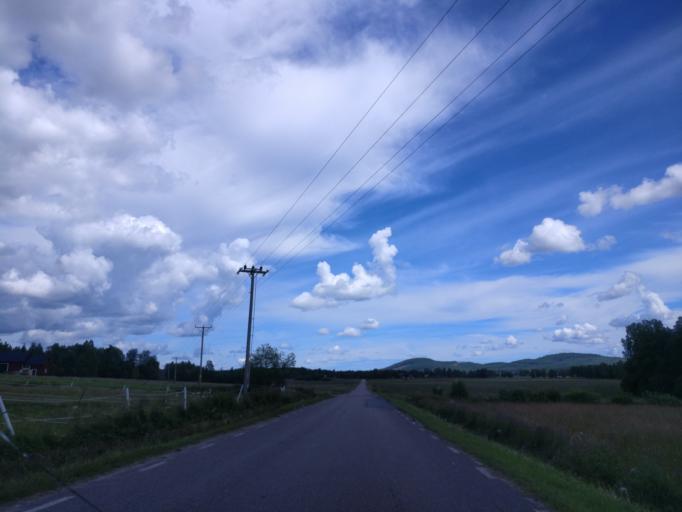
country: SE
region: Vaermland
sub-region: Hagfors Kommun
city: Ekshaerad
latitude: 60.1205
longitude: 13.4523
